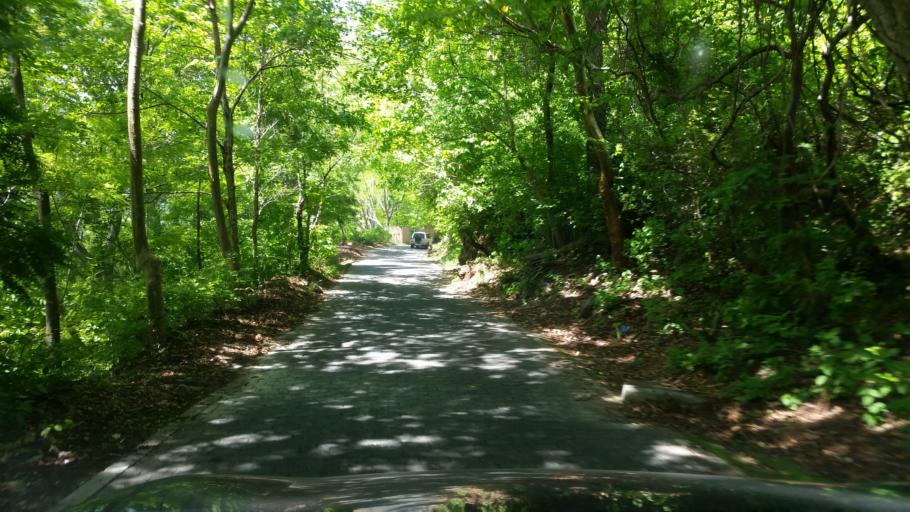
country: NI
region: Masaya
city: Catarina
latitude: 11.9229
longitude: -86.0573
